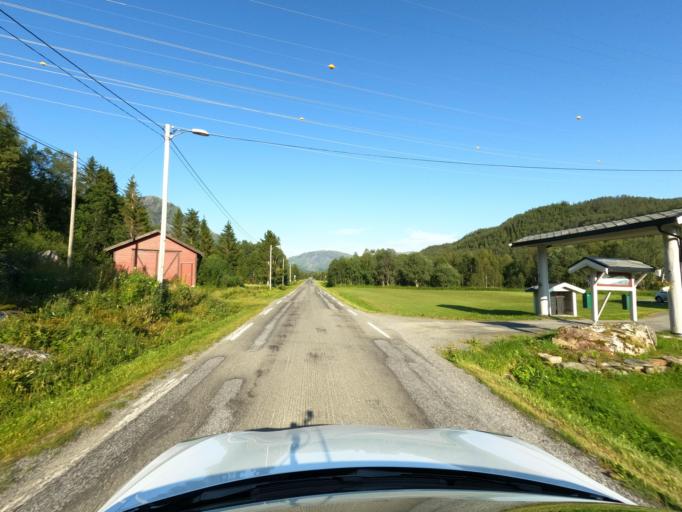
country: NO
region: Nordland
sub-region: Narvik
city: Bjerkvik
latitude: 68.5577
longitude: 17.6263
